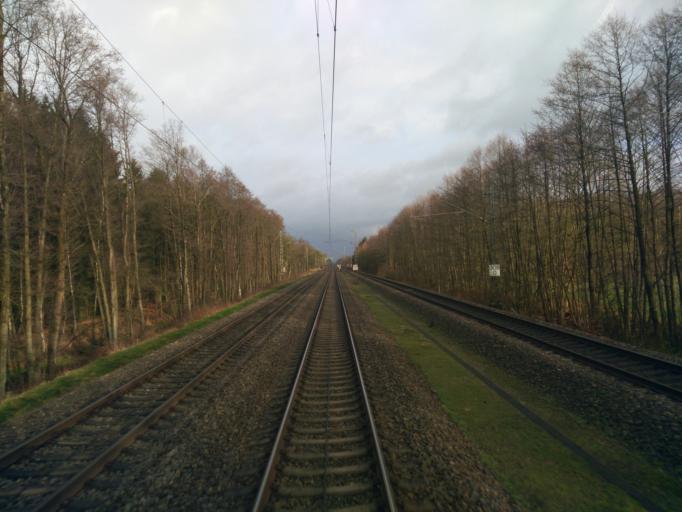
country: DE
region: Lower Saxony
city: Wistedt
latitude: 53.2515
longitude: 9.6875
